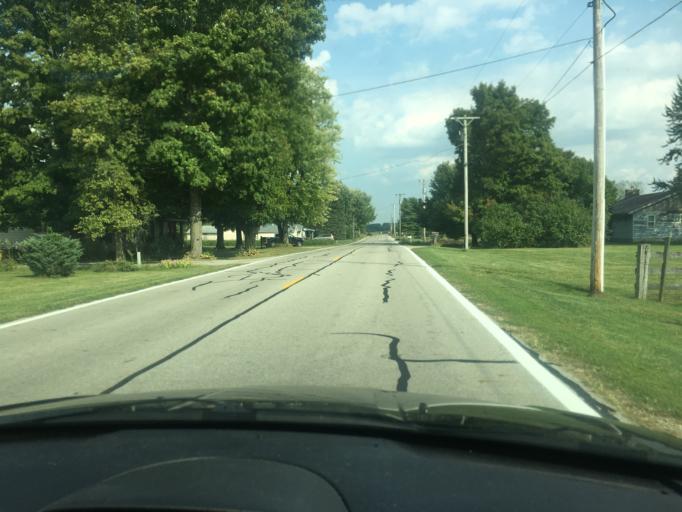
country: US
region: Ohio
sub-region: Champaign County
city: Urbana
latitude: 40.1277
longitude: -83.7768
